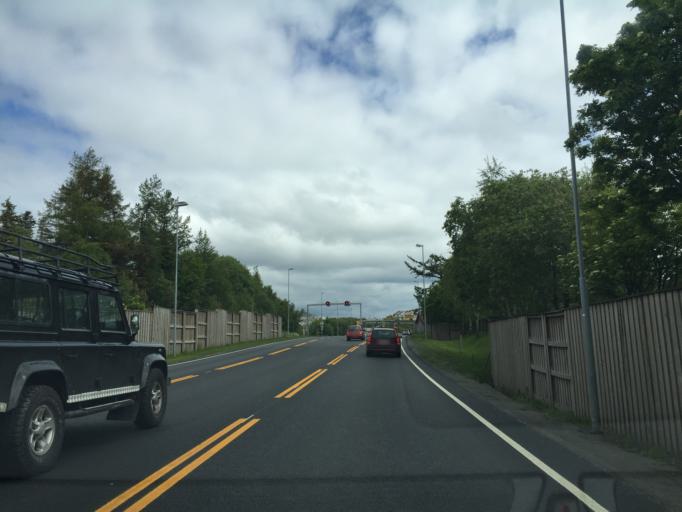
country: NO
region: Nordland
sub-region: Bodo
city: Lopsmarka
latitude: 67.2776
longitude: 14.4729
